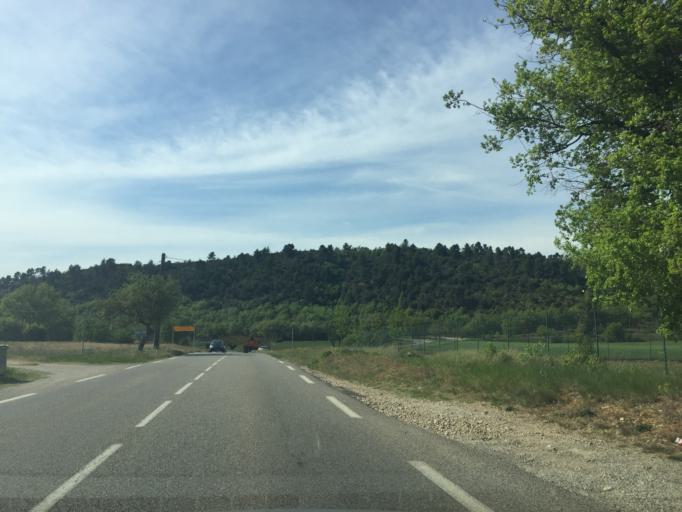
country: FR
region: Provence-Alpes-Cote d'Azur
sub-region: Departement du Var
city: Vinon-sur-Verdon
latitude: 43.7042
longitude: 5.8253
